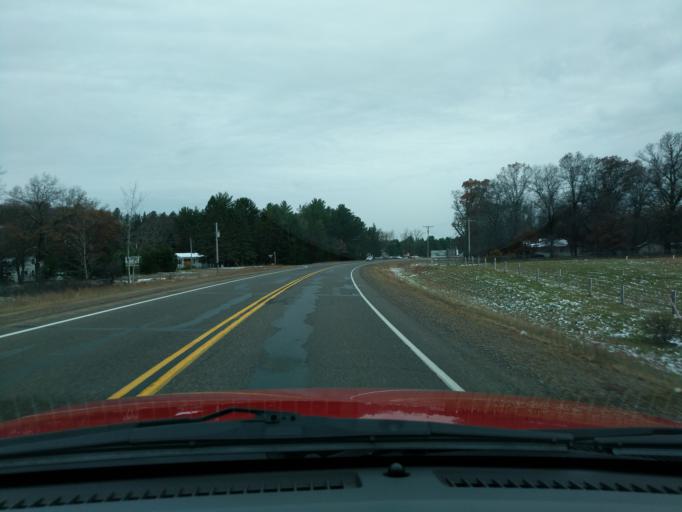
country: US
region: Wisconsin
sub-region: Burnett County
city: Siren
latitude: 45.8172
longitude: -92.3409
